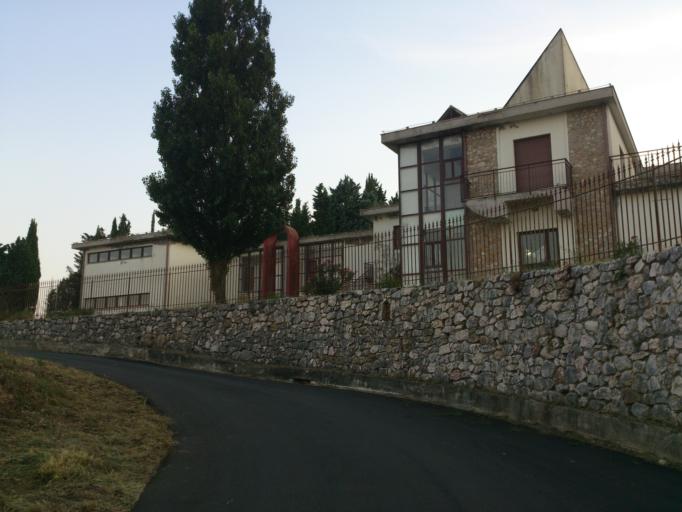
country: IT
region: Calabria
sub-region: Provincia di Reggio Calabria
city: Pazzano
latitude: 38.4705
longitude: 16.4499
